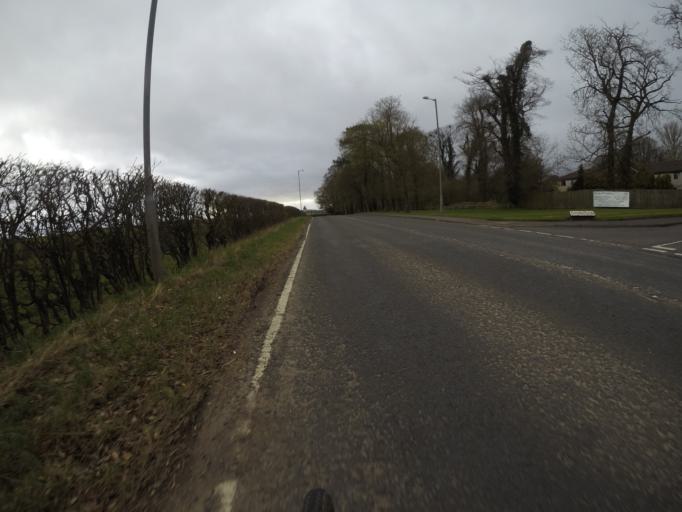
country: GB
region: Scotland
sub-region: East Ayrshire
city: Crosshouse
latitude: 55.6116
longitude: -4.5724
